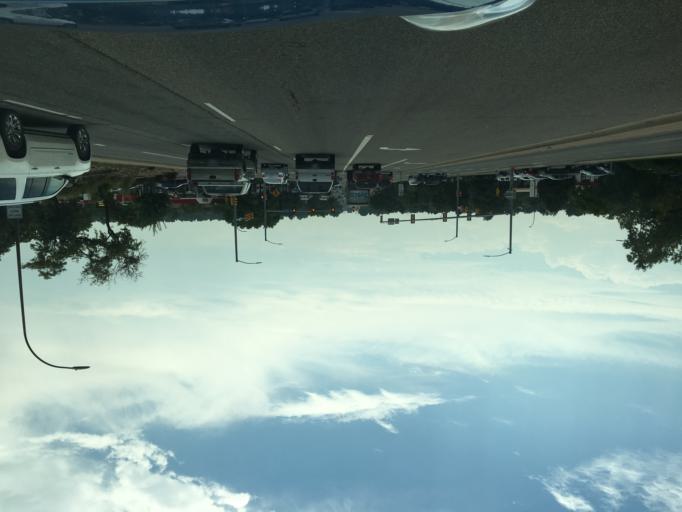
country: US
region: Colorado
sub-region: Jefferson County
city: Arvada
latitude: 39.8429
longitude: -105.0819
